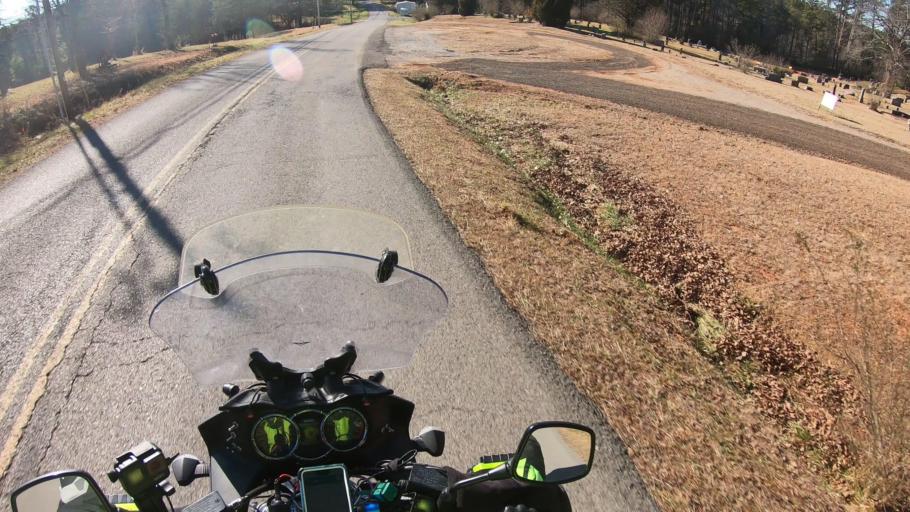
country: US
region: Georgia
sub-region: Fannin County
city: McCaysville
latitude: 34.9969
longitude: -84.3321
